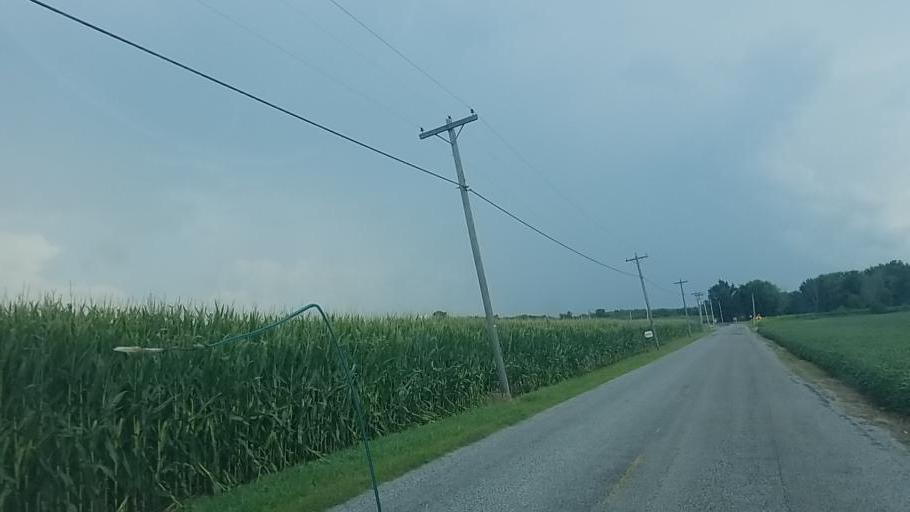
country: US
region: Ohio
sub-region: Medina County
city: Lodi
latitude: 41.0034
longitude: -82.0189
